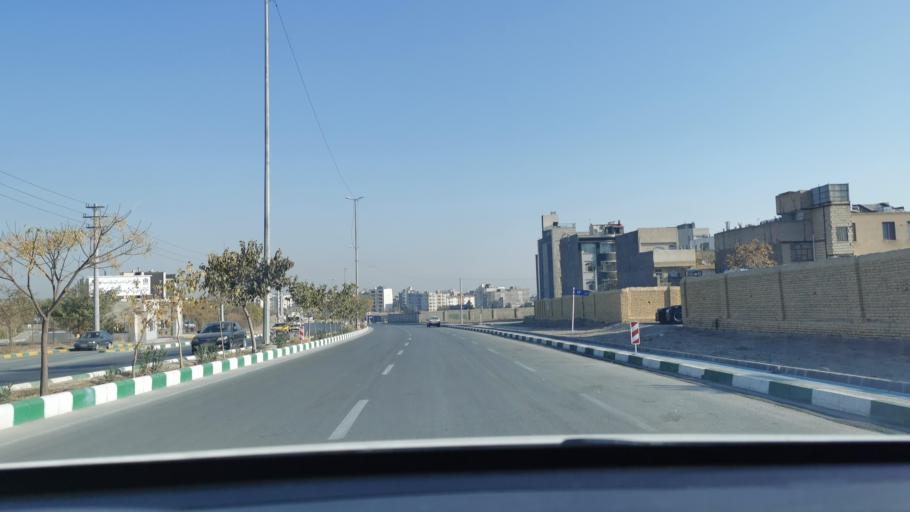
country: IR
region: Razavi Khorasan
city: Mashhad
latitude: 36.2779
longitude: 59.5407
